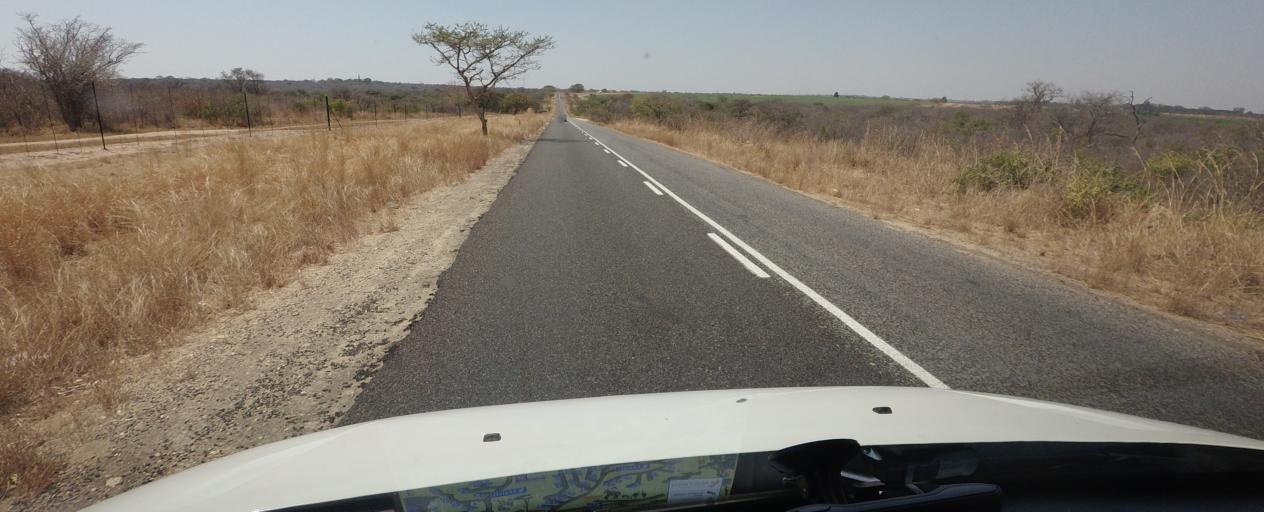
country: ZA
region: Limpopo
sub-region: Mopani District Municipality
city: Hoedspruit
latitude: -24.5372
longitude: 31.0096
